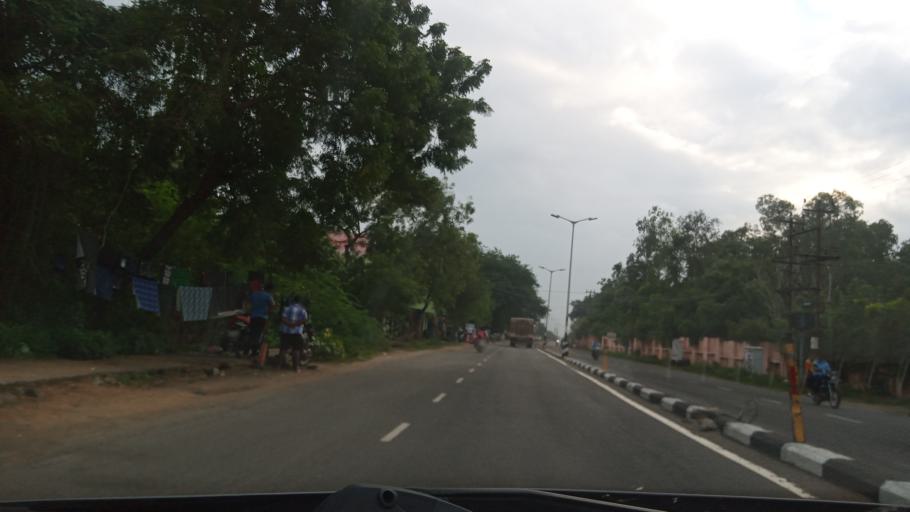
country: IN
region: Tamil Nadu
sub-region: Villupuram
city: Auroville
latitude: 12.0185
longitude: 79.8595
